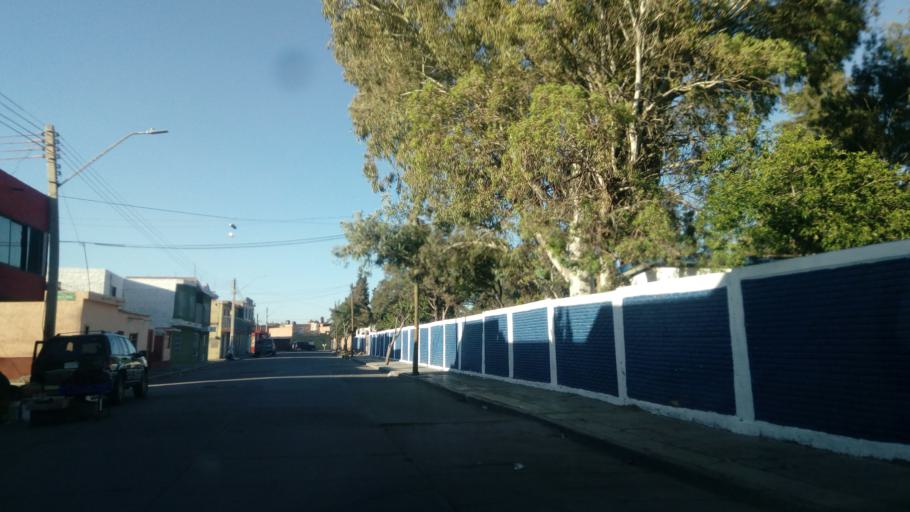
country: MX
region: Durango
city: Victoria de Durango
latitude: 23.9993
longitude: -104.6785
